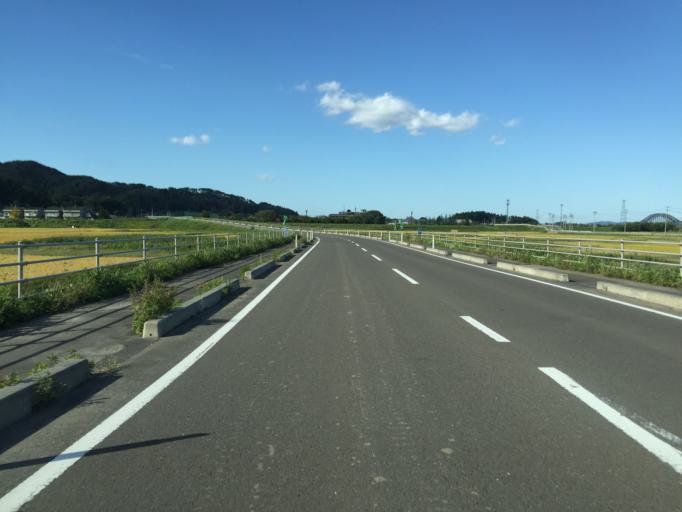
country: JP
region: Miyagi
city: Marumori
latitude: 37.9041
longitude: 140.7659
